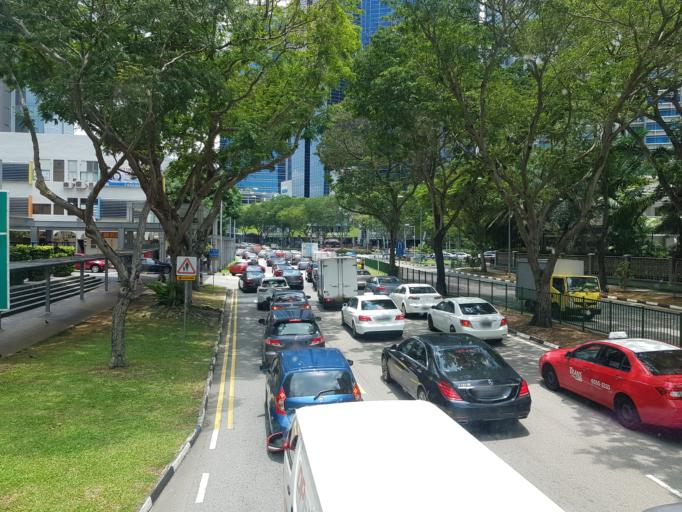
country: SG
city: Singapore
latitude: 1.3174
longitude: 103.8441
